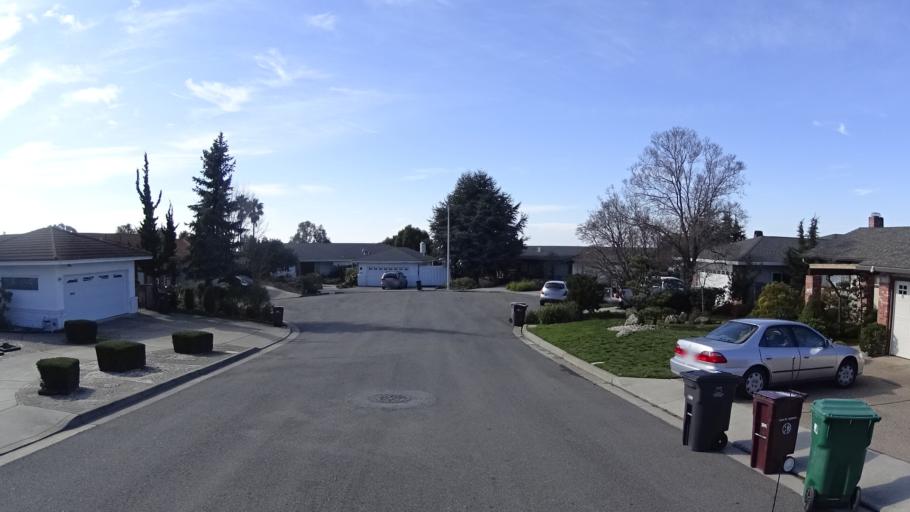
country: US
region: California
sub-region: Alameda County
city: Fairview
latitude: 37.6612
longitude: -122.0393
